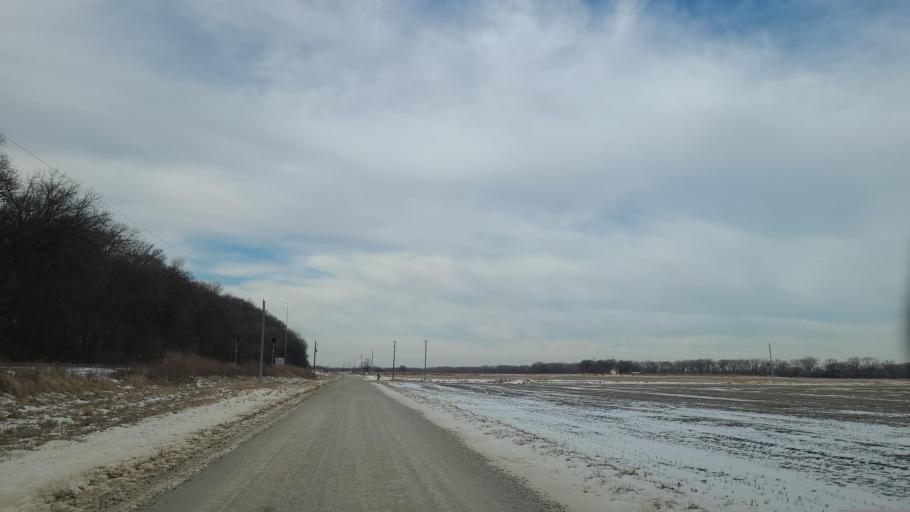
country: US
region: Kansas
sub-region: Jefferson County
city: Oskaloosa
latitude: 39.0615
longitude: -95.4359
